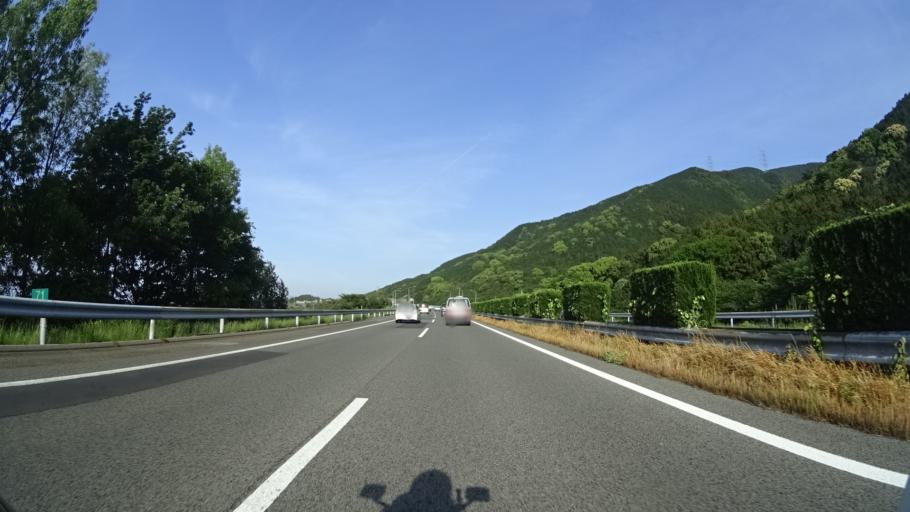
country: JP
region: Ehime
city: Kawanoecho
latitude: 33.9556
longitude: 133.4649
